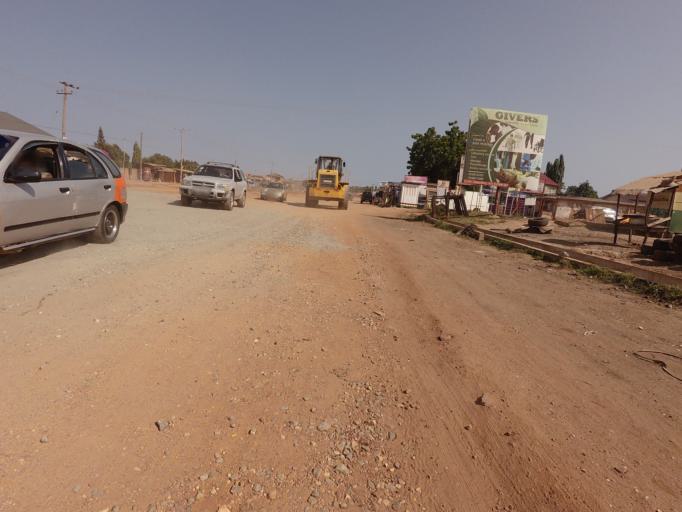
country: GH
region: Greater Accra
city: Teshi Old Town
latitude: 5.6088
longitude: -0.1231
